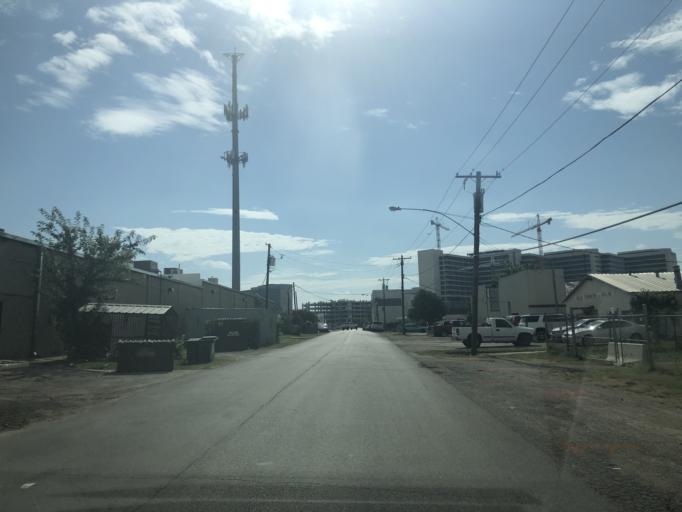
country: US
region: Texas
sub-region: Dallas County
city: Dallas
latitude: 32.8213
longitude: -96.8556
